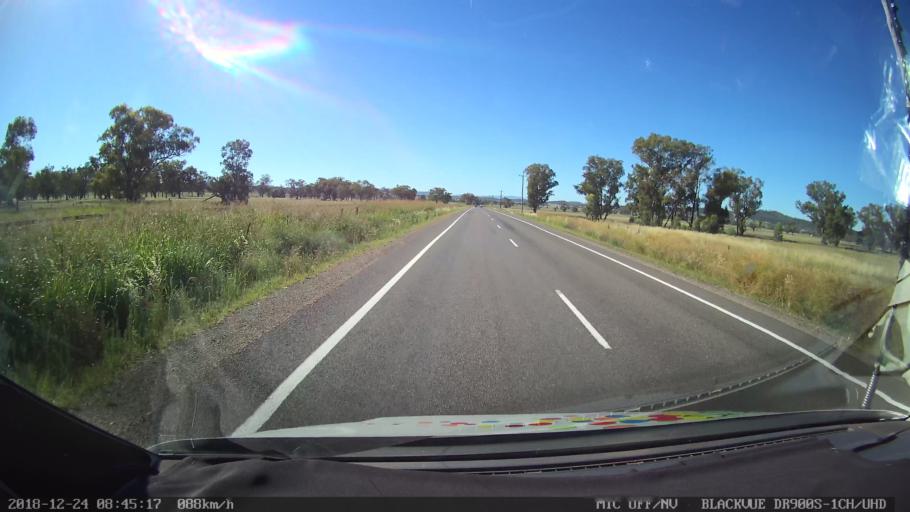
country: AU
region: New South Wales
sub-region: Liverpool Plains
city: Quirindi
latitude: -31.4129
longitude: 150.6514
